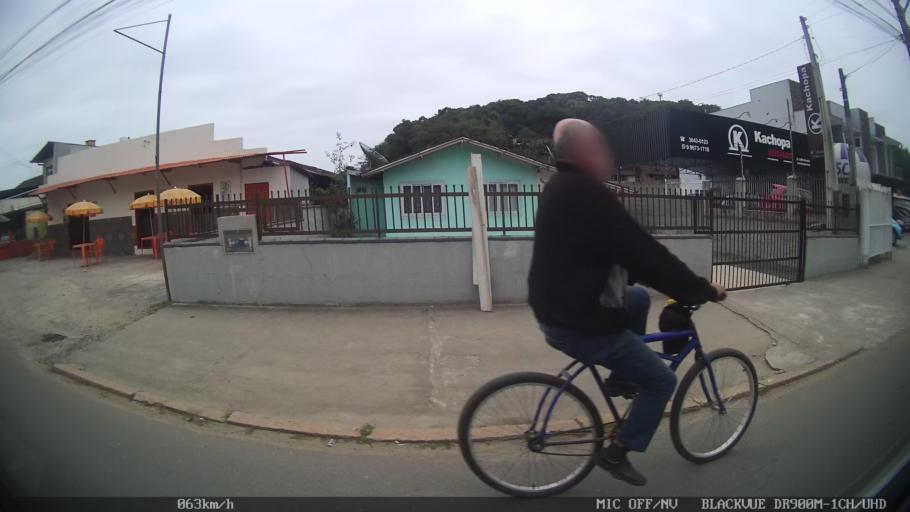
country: BR
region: Santa Catarina
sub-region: Joinville
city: Joinville
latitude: -26.3373
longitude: -48.8266
